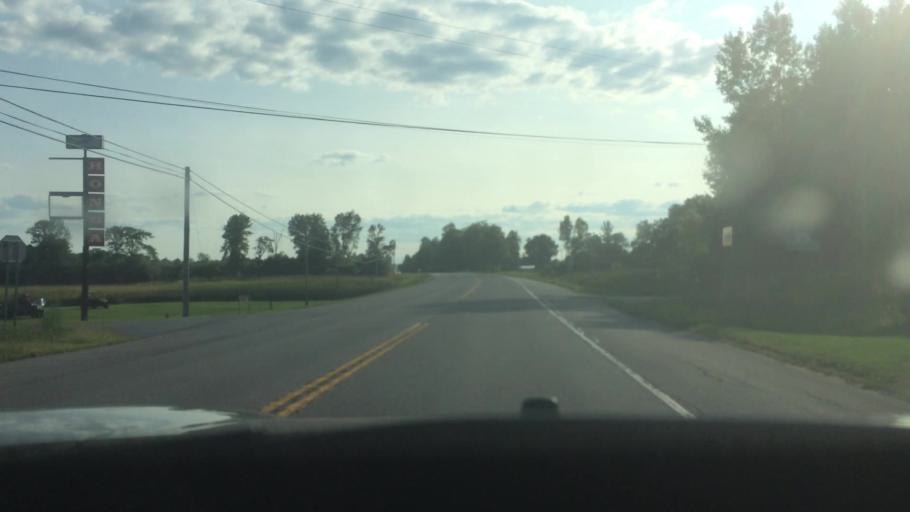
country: US
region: New York
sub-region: St. Lawrence County
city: Canton
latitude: 44.6318
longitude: -75.0844
